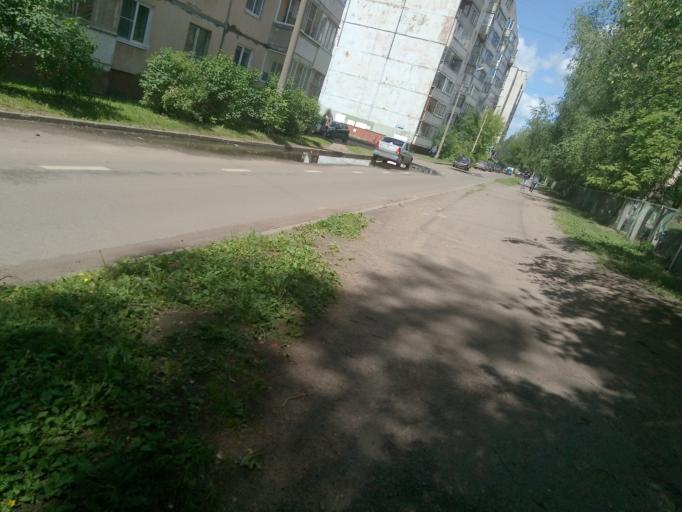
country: RU
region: Jaroslavl
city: Yaroslavl
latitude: 57.6509
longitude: 39.9637
